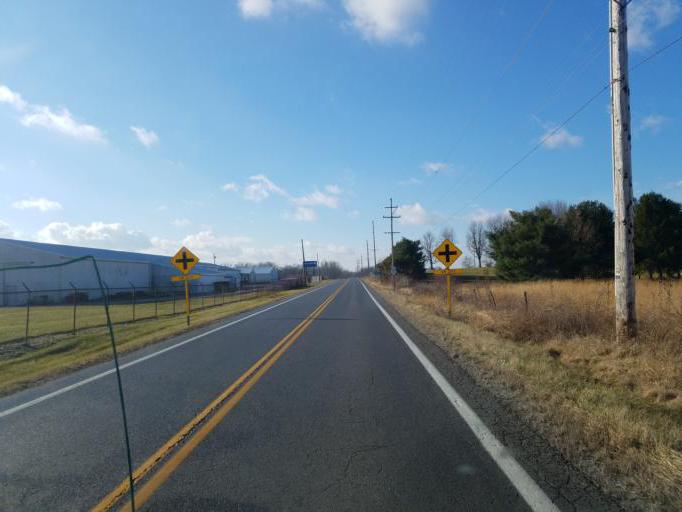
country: US
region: Ohio
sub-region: Marion County
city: Marion
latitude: 40.5510
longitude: -83.1903
